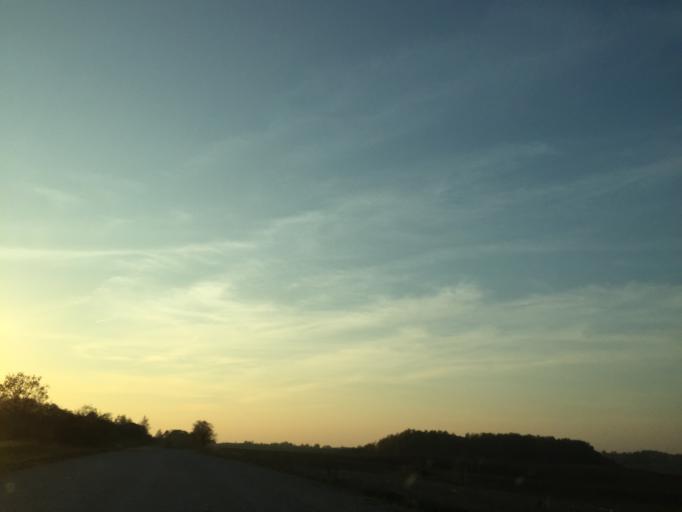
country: LV
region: Priekule
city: Priekule
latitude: 56.4730
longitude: 21.6168
